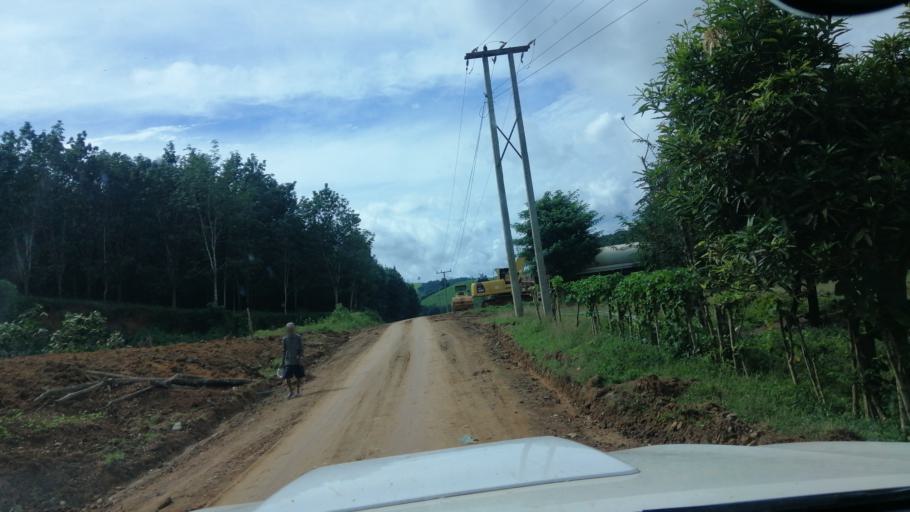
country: TH
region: Phayao
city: Phu Sang
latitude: 19.6393
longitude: 100.5256
